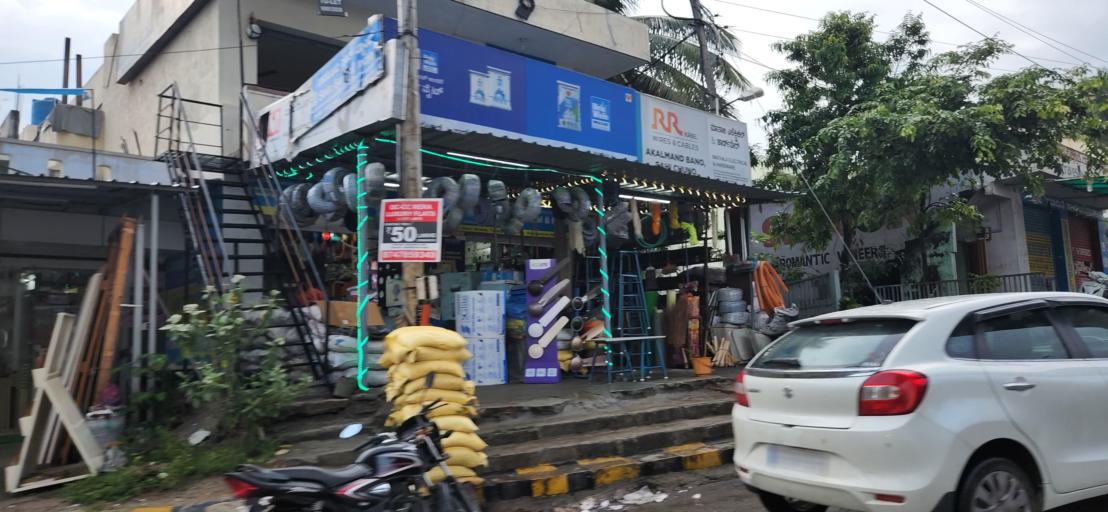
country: IN
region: Karnataka
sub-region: Bangalore Urban
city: Bangalore
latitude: 12.8672
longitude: 77.5351
